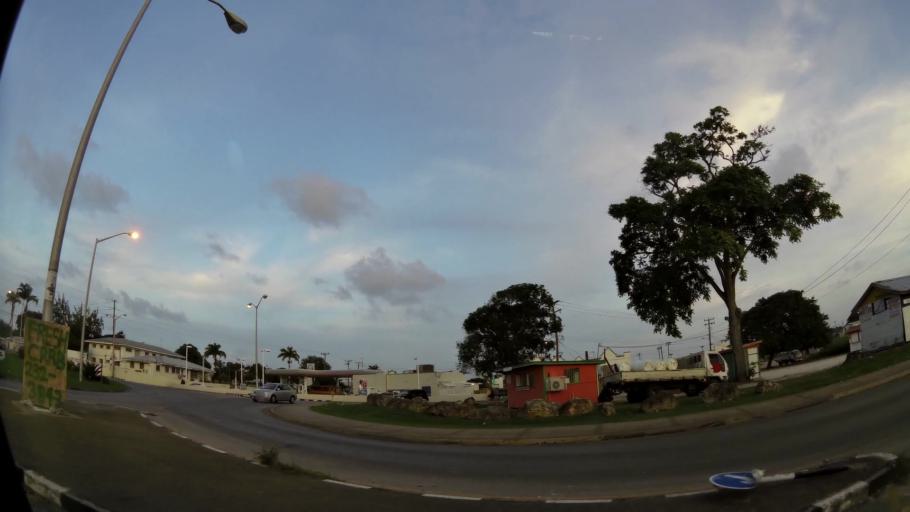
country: BB
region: Saint Philip
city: Crane
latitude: 13.1175
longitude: -59.4772
